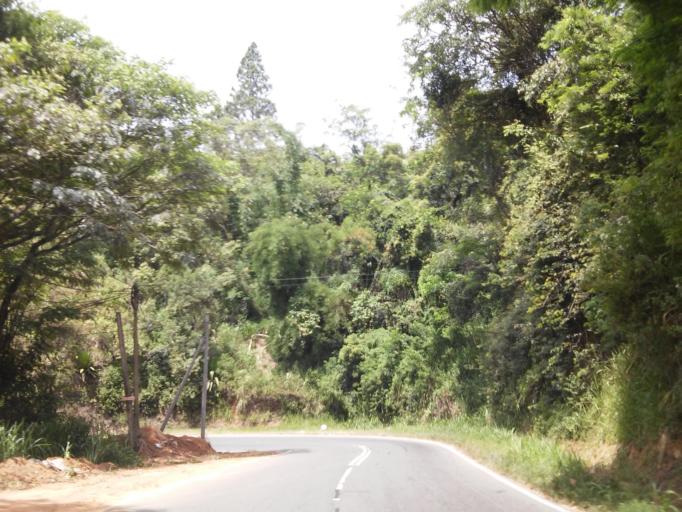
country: LK
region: Uva
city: Haputale
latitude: 6.8691
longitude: 80.9516
